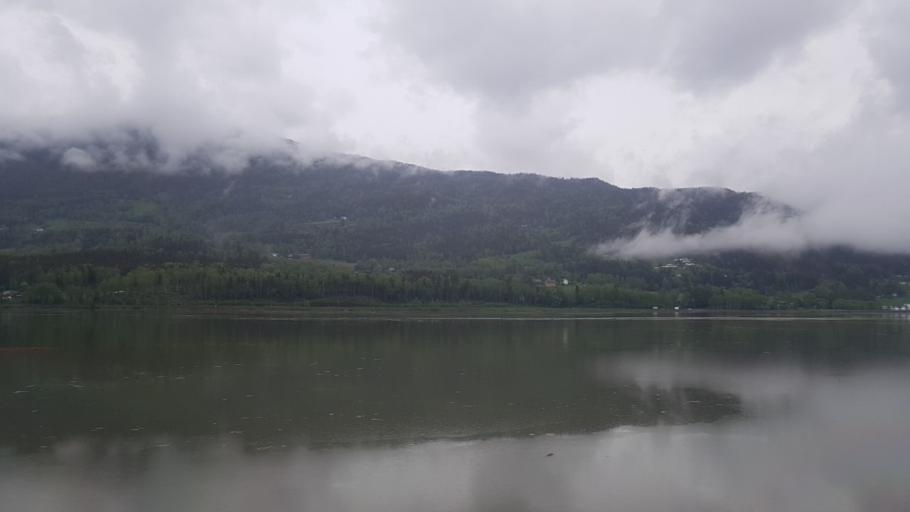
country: NO
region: Oppland
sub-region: Oyer
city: Tretten
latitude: 61.3897
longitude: 10.2549
